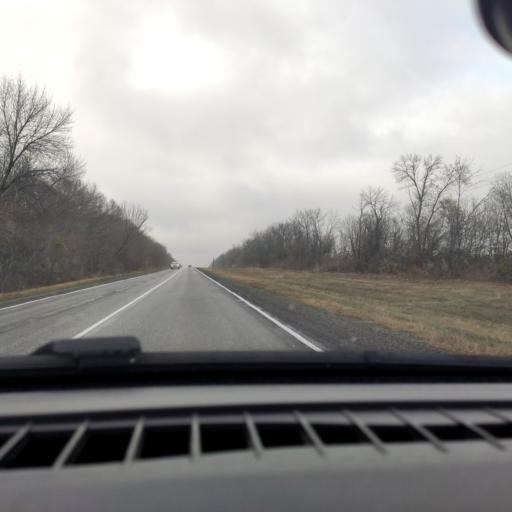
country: RU
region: Voronezj
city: Uryv-Pokrovka
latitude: 51.1070
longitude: 39.0218
